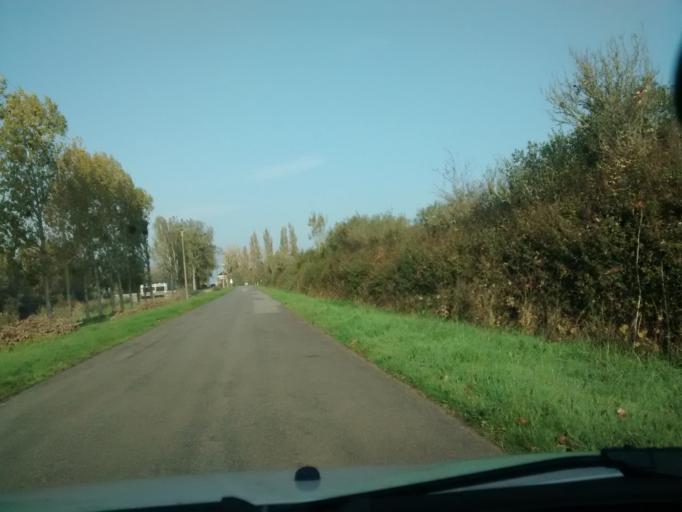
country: FR
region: Pays de la Loire
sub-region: Departement de la Loire-Atlantique
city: Vue
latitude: 47.2367
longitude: -1.8672
